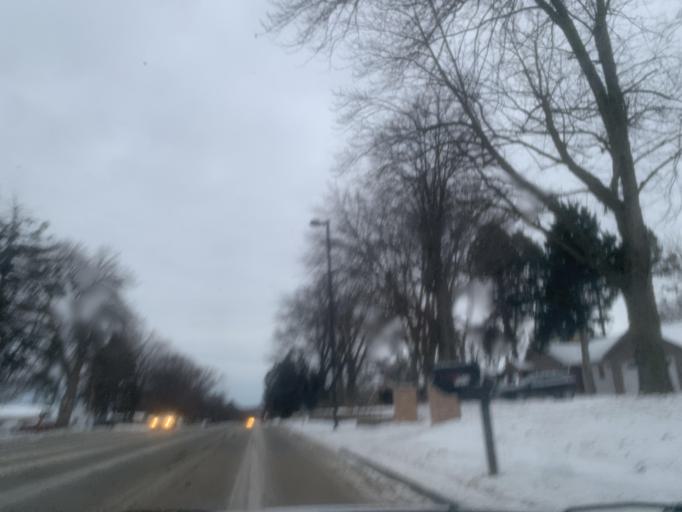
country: US
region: Nebraska
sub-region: Douglas County
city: Ralston
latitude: 41.2470
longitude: -96.0527
